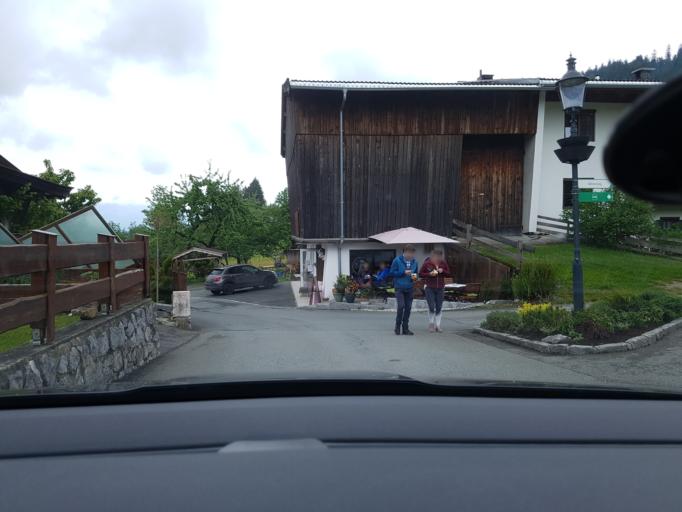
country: AT
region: Tyrol
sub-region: Politischer Bezirk Kufstein
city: Ellmau
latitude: 47.5138
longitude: 12.3294
